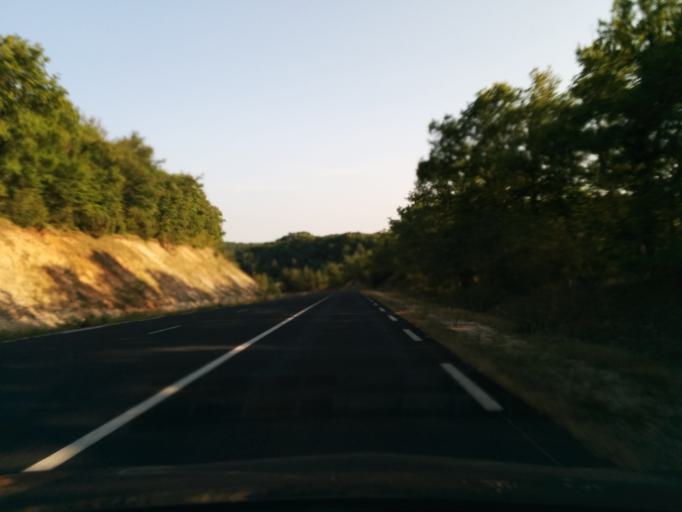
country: FR
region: Midi-Pyrenees
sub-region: Departement du Lot
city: Le Vigan
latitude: 44.7167
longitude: 1.4818
